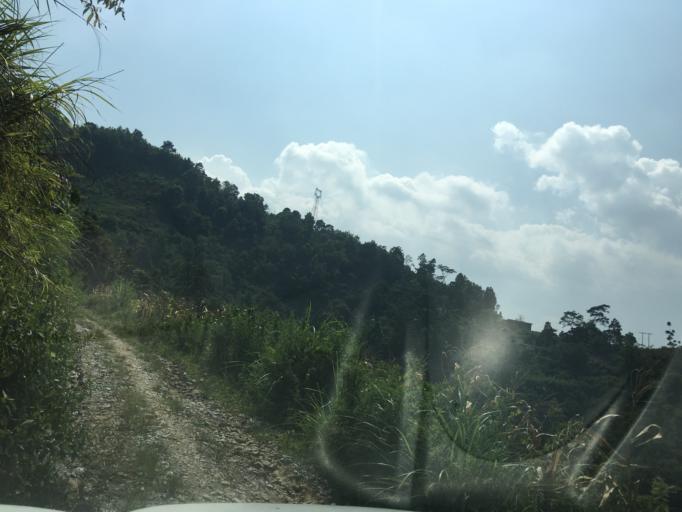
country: CN
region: Guangxi Zhuangzu Zizhiqu
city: Xinzhou
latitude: 24.9905
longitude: 105.7431
